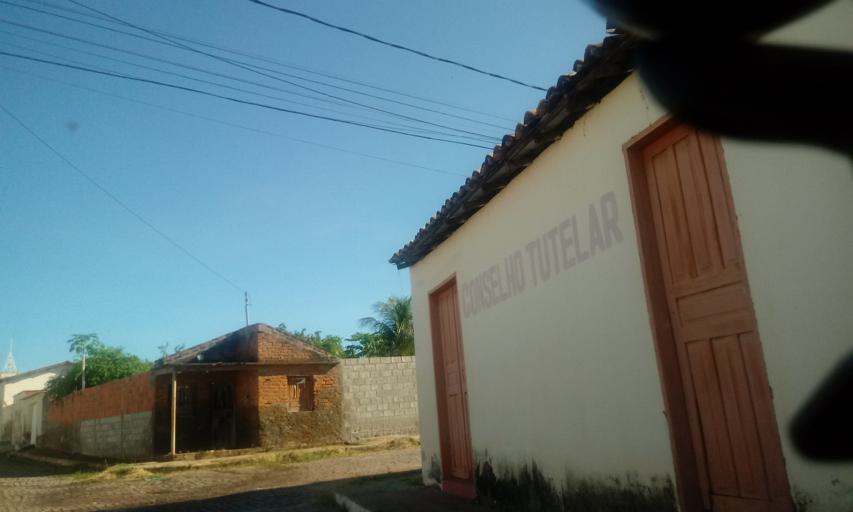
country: BR
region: Bahia
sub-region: Riacho De Santana
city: Riacho de Santana
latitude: -13.9117
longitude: -42.8452
